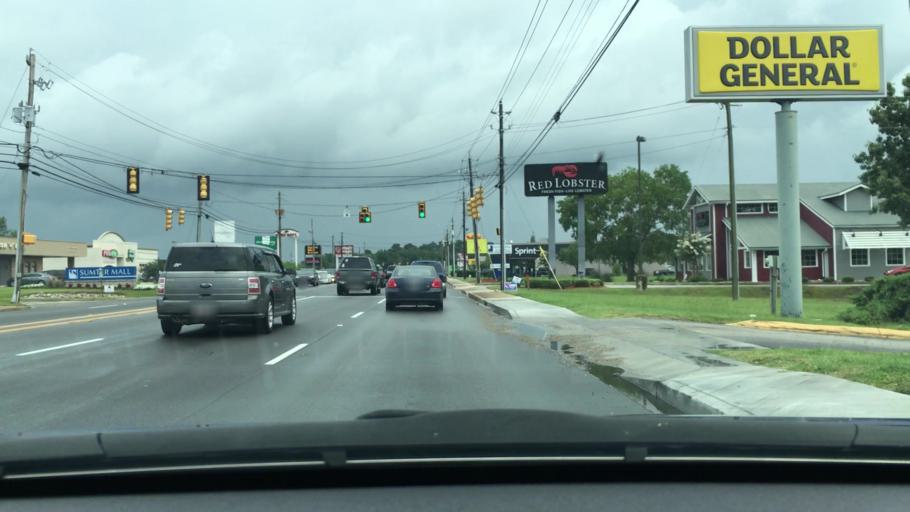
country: US
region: South Carolina
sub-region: Sumter County
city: Sumter
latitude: 33.9482
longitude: -80.3749
